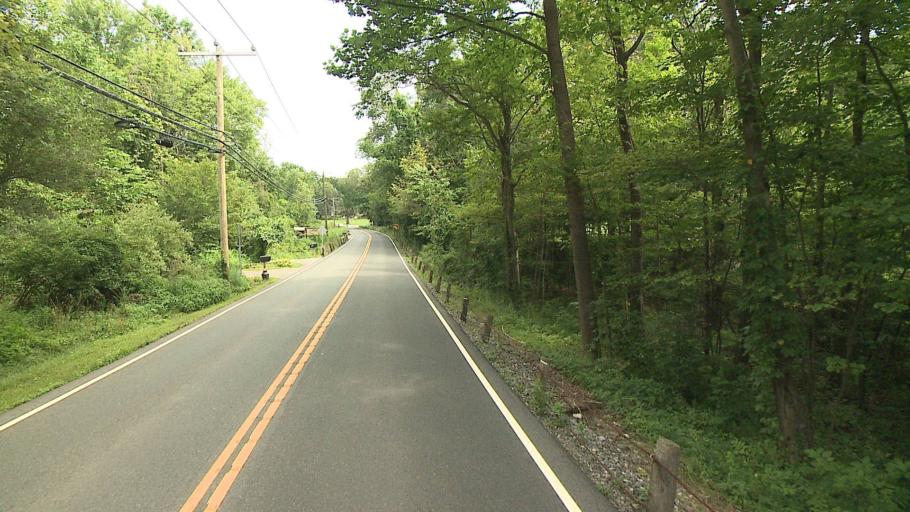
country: US
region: Connecticut
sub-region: Fairfield County
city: Sherman
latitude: 41.5015
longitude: -73.4698
